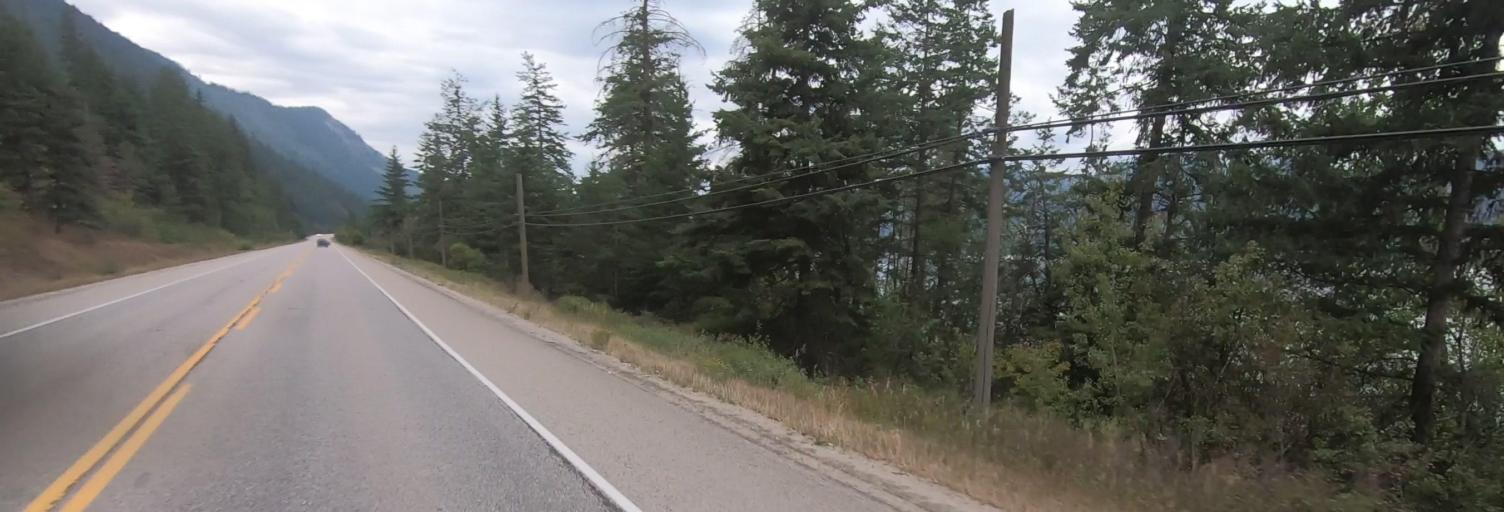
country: CA
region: British Columbia
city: Chase
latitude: 50.8503
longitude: -119.6123
